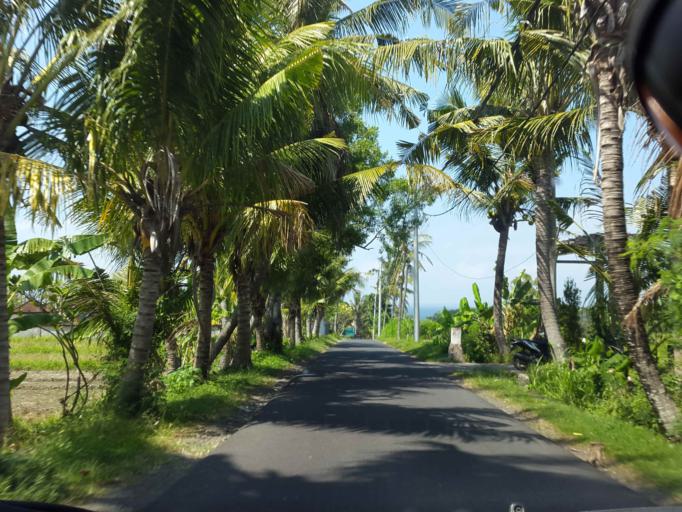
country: ID
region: Bali
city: Klungkung
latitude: -8.5656
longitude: 115.3733
